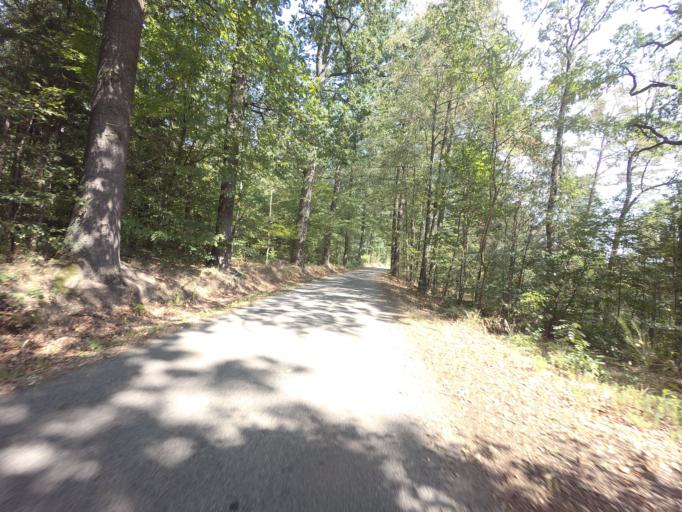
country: CZ
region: Jihocesky
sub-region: Okres Ceske Budejovice
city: Hluboka nad Vltavou
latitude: 49.0635
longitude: 14.4479
